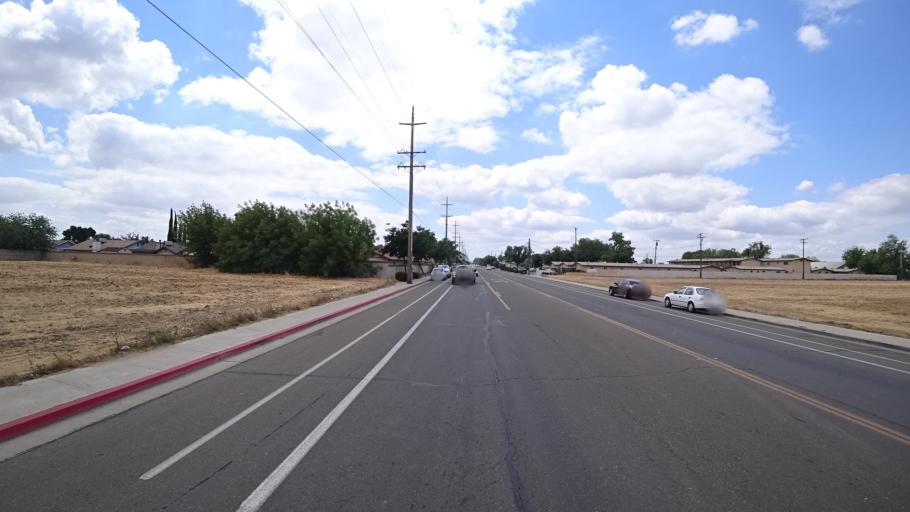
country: US
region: California
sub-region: Kings County
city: Hanford
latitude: 36.3134
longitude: -119.6560
